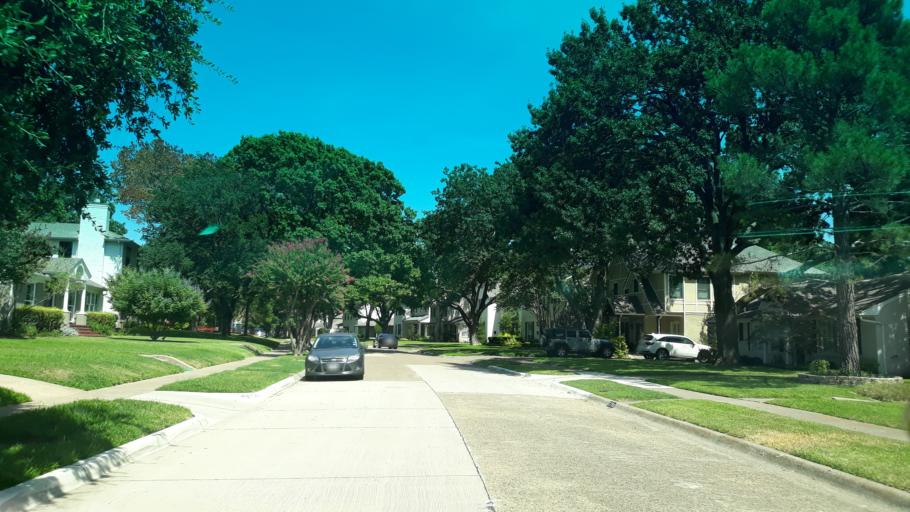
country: US
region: Texas
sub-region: Dallas County
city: Highland Park
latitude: 32.8302
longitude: -96.7447
